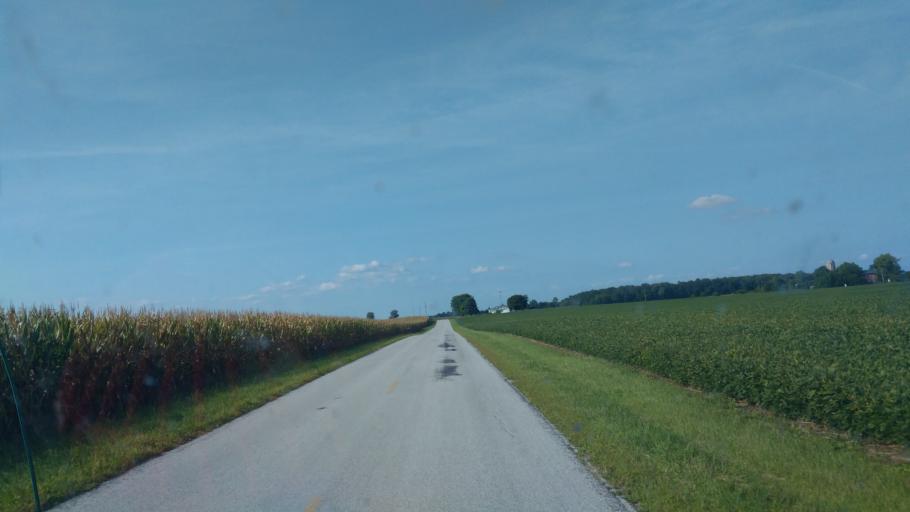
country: US
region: Ohio
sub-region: Hardin County
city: Kenton
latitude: 40.7200
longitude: -83.5725
